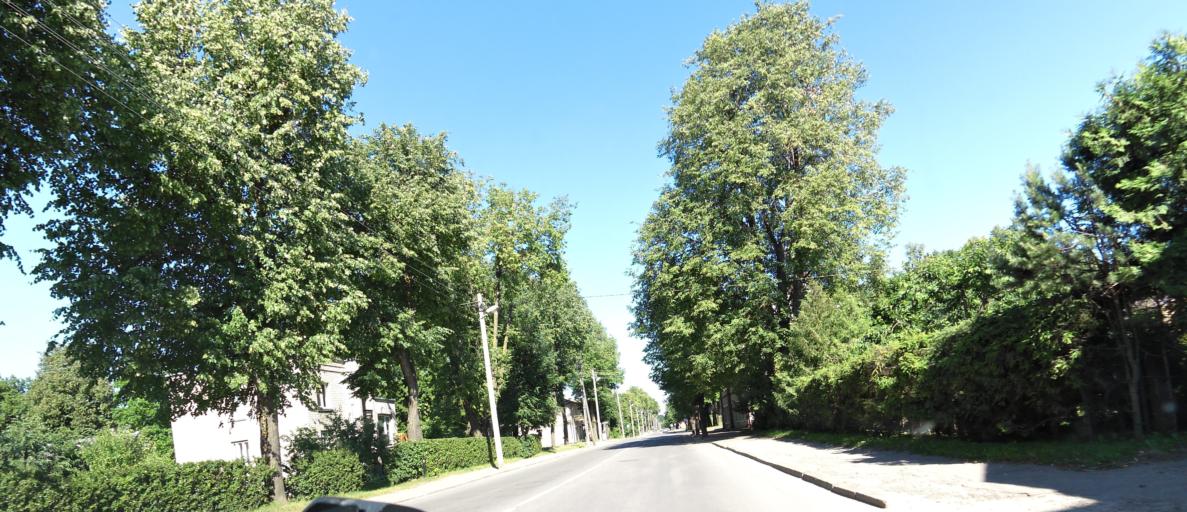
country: LT
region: Panevezys
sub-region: Birzai
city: Birzai
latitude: 56.2018
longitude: 24.7457
